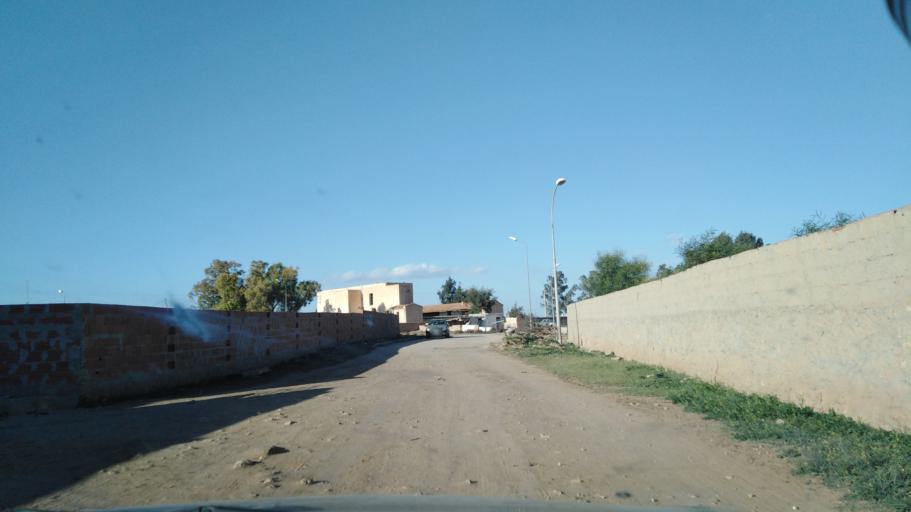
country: TN
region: Al Mahdiyah
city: Shurban
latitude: 34.9592
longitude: 10.3630
